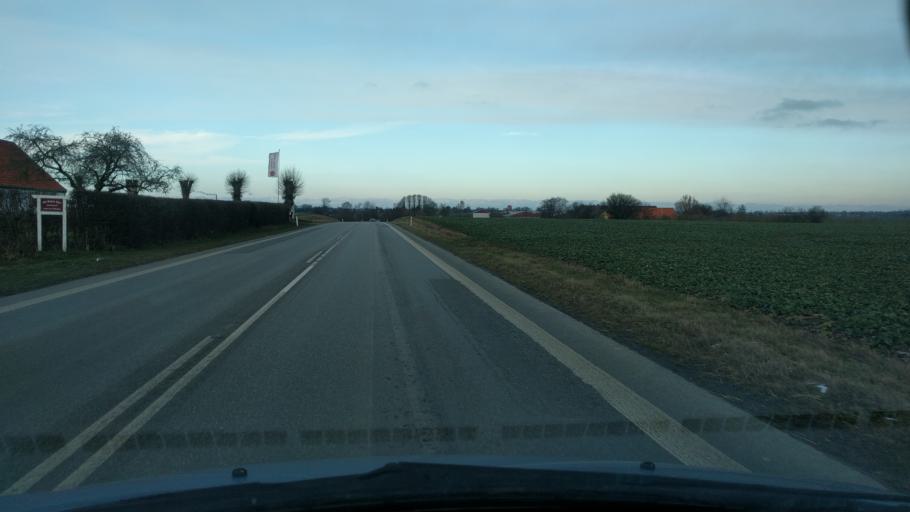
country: DK
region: Zealand
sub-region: Guldborgsund Kommune
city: Stubbekobing
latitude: 54.8736
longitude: 12.0261
